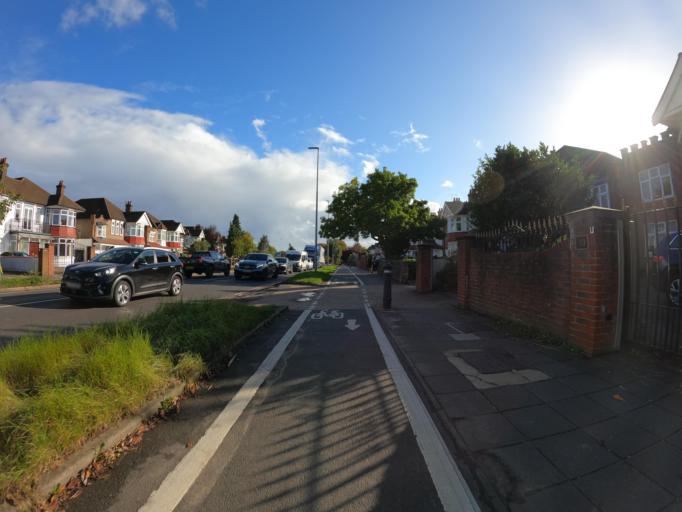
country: GB
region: England
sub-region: Greater London
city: Acton
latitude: 51.5043
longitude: -0.2896
